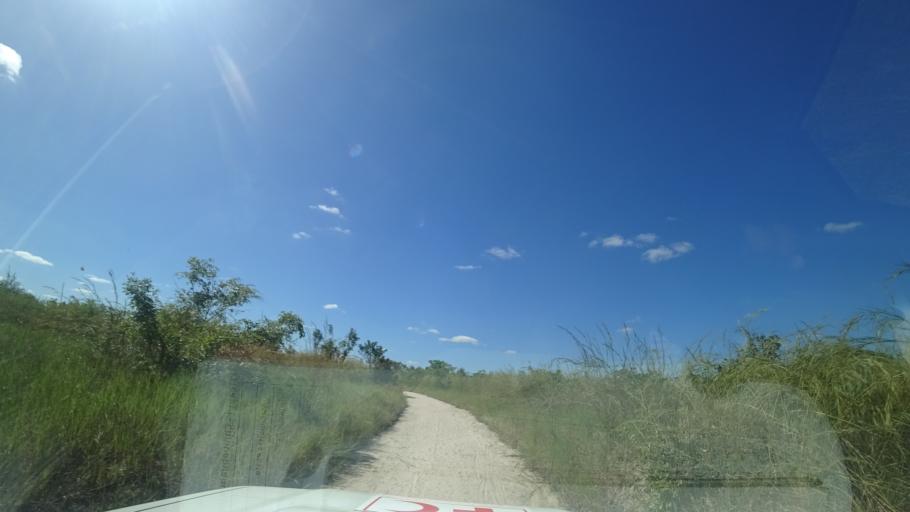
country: MZ
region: Sofala
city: Dondo
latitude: -19.4806
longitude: 34.6259
